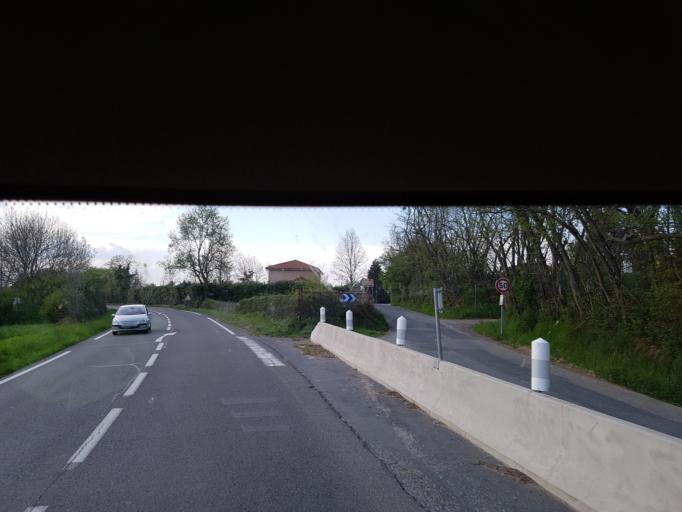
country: FR
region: Rhone-Alpes
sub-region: Departement du Rhone
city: Lentilly
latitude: 45.8055
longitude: 4.6679
